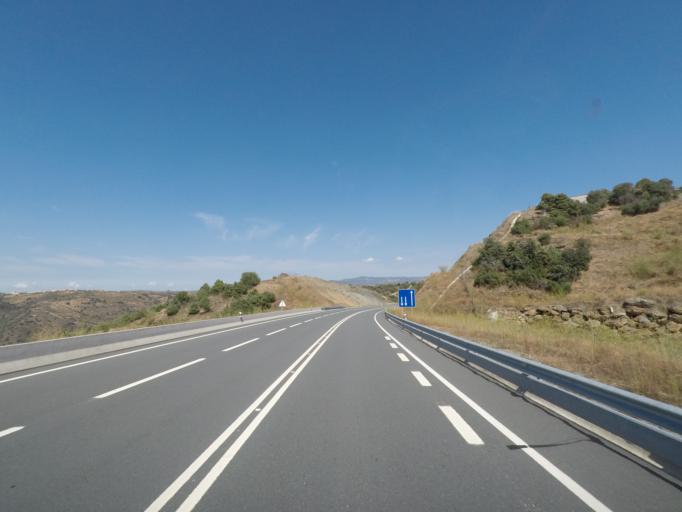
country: PT
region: Braganca
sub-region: Alfandega da Fe
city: Alfandega da Fe
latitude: 41.2879
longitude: -6.8949
